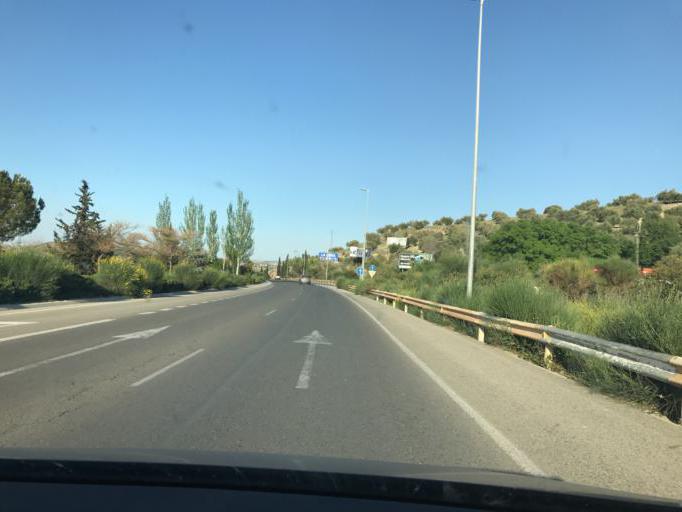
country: ES
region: Andalusia
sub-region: Provincia de Jaen
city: Jaen
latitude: 37.7740
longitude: -3.7637
